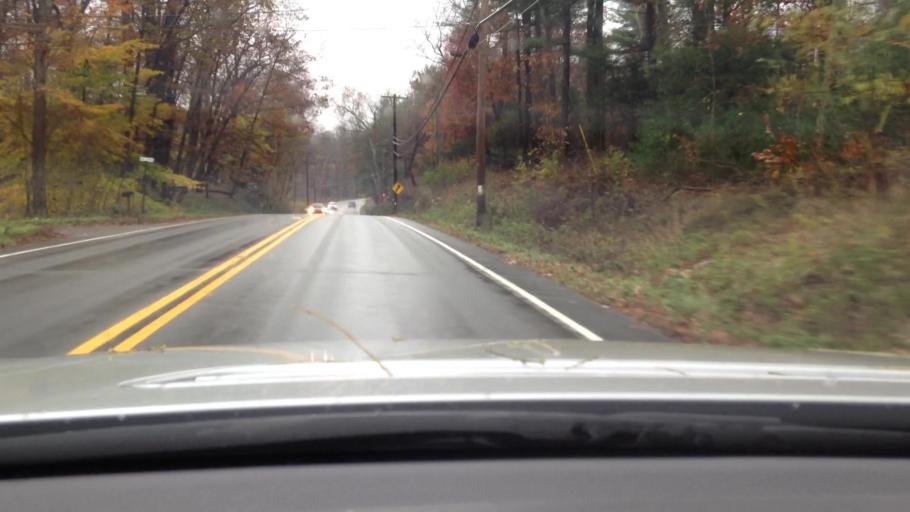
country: US
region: New York
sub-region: Orange County
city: West Point
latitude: 41.3991
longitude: -73.9332
